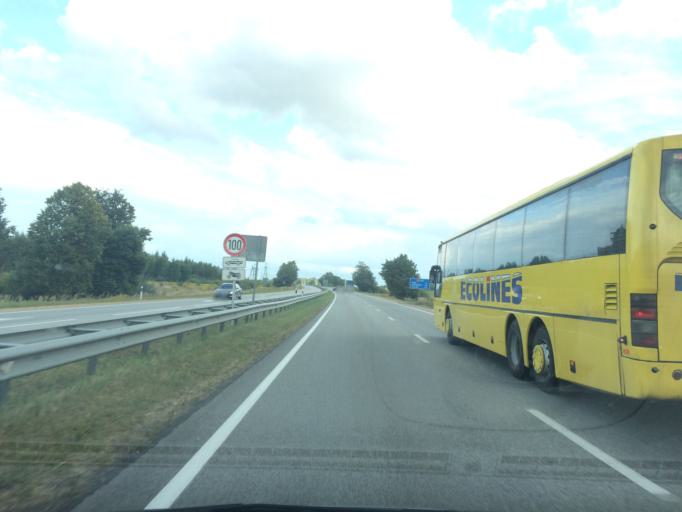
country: LV
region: Salaspils
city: Salaspils
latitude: 56.8467
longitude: 24.3620
